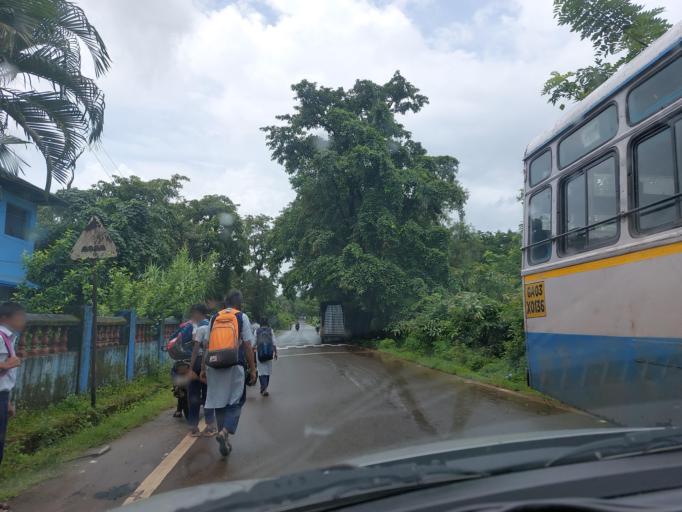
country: IN
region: Goa
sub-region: North Goa
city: Valpoy
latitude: 15.5410
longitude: 74.1371
